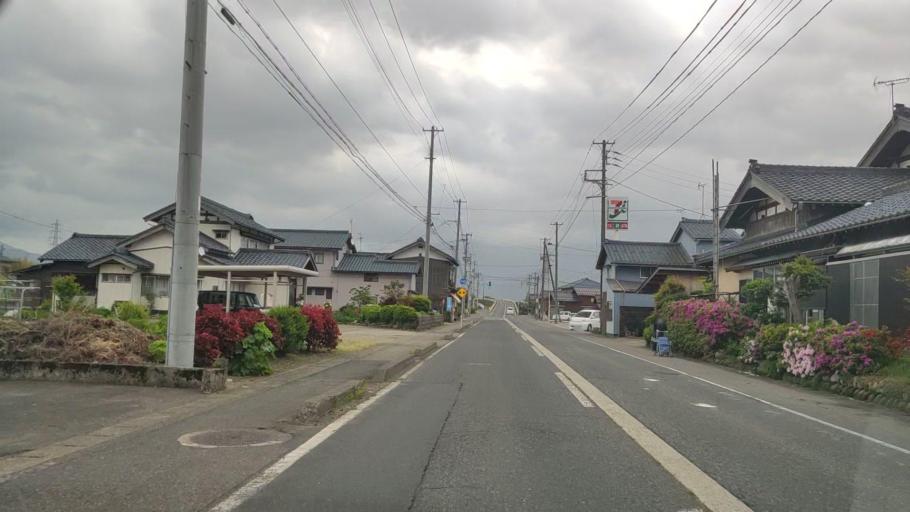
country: JP
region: Niigata
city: Gosen
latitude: 37.7336
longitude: 139.1979
